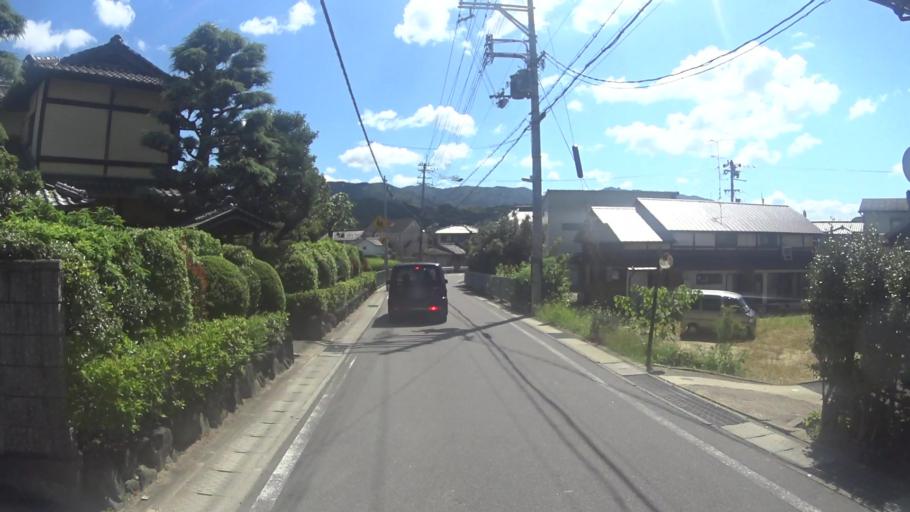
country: JP
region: Kyoto
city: Tanabe
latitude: 34.8322
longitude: 135.8020
